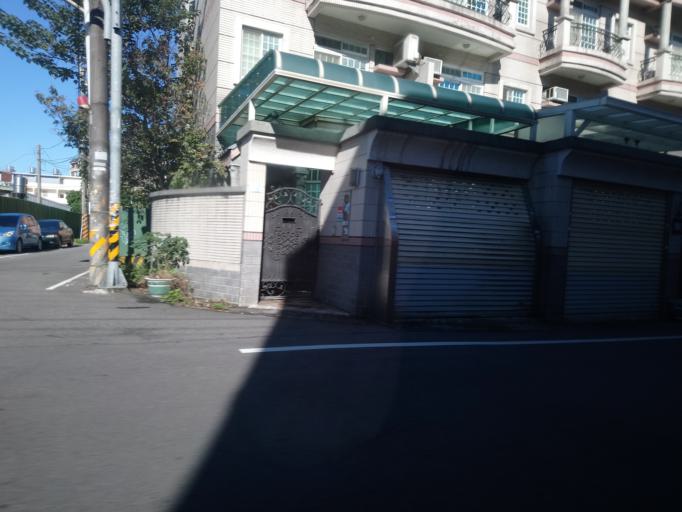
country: TW
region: Taiwan
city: Daxi
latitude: 24.9024
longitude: 121.2764
